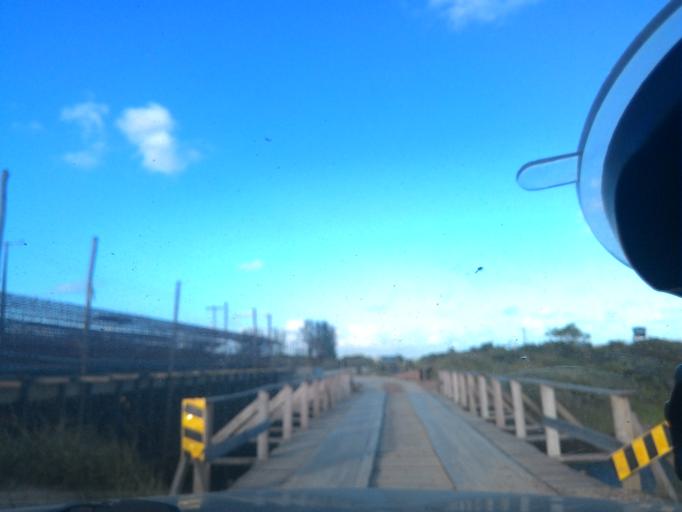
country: BR
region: Sao Paulo
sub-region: Pariquera-Acu
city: Pariquera Acu
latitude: -24.8715
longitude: -47.7236
